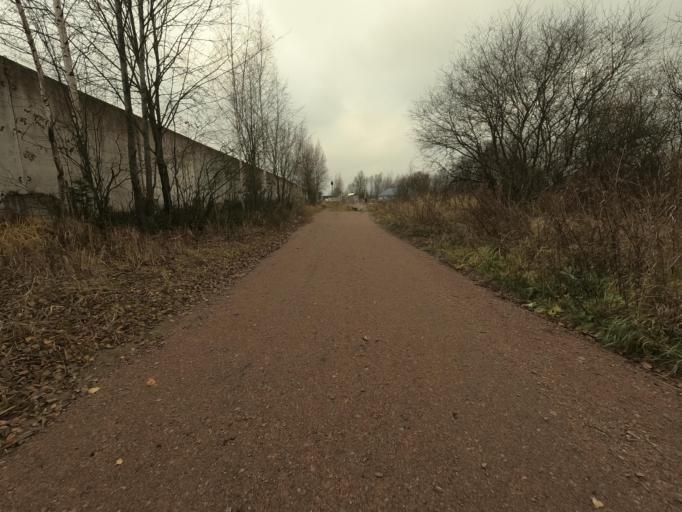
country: RU
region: Leningrad
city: Lyuban'
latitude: 59.4928
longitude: 31.2730
